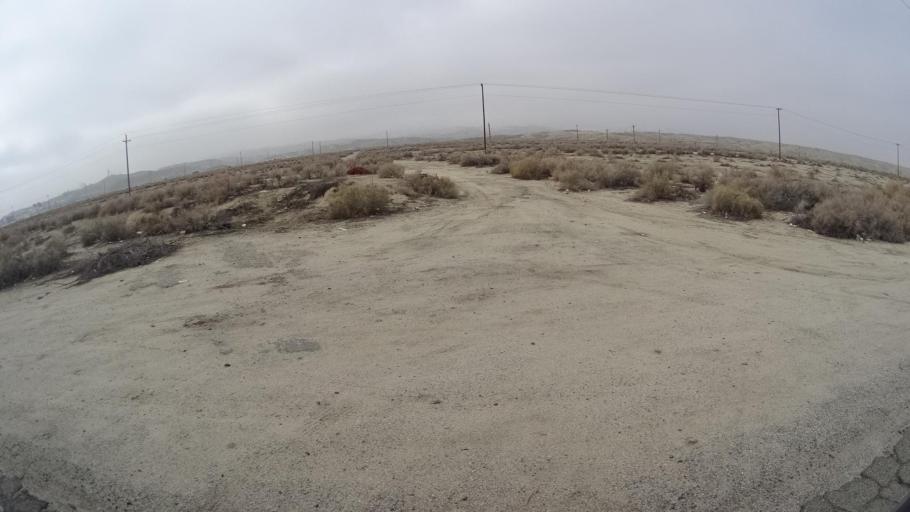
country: US
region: California
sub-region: Kern County
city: Maricopa
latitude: 35.0971
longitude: -119.4022
